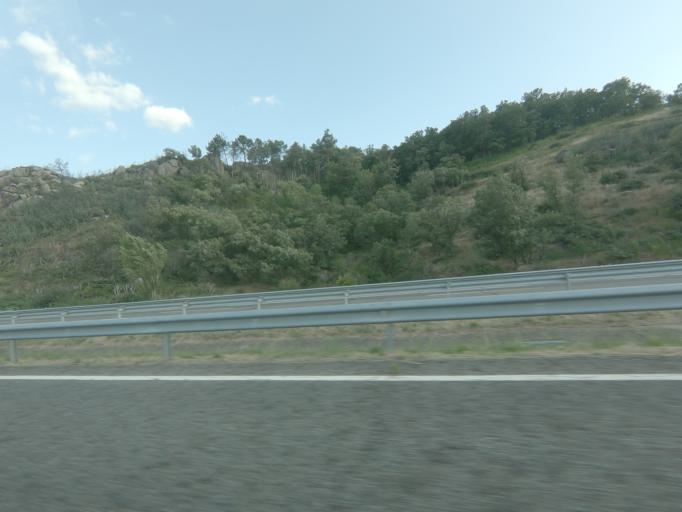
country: ES
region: Galicia
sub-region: Provincia de Ourense
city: Oimbra
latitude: 41.9256
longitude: -7.4872
